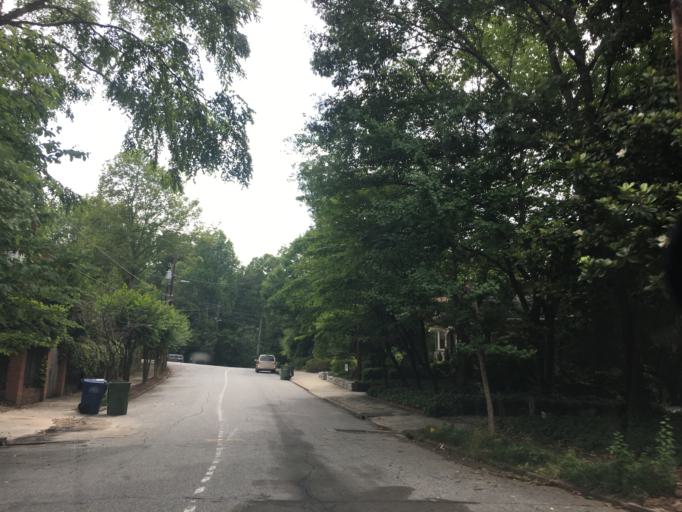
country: US
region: Georgia
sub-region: DeKalb County
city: Druid Hills
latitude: 33.7925
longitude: -84.3765
